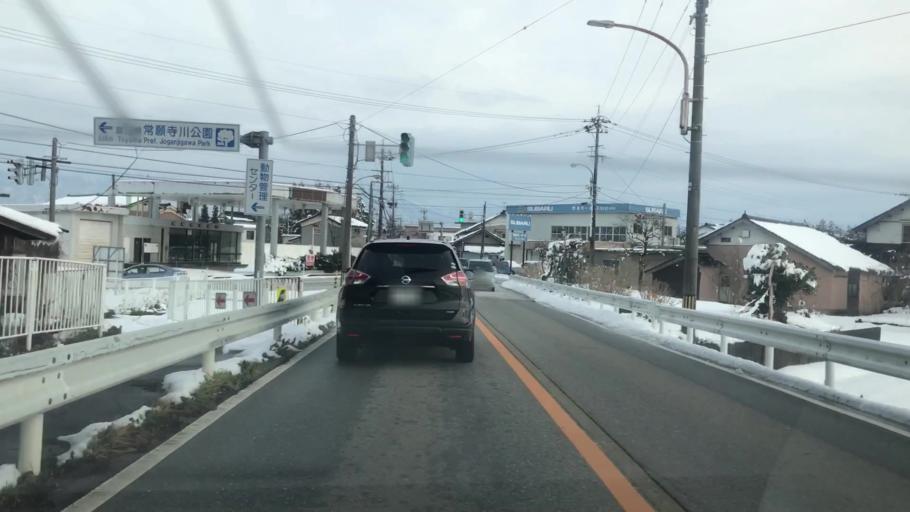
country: JP
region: Toyama
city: Toyama-shi
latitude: 36.6716
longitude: 137.2882
